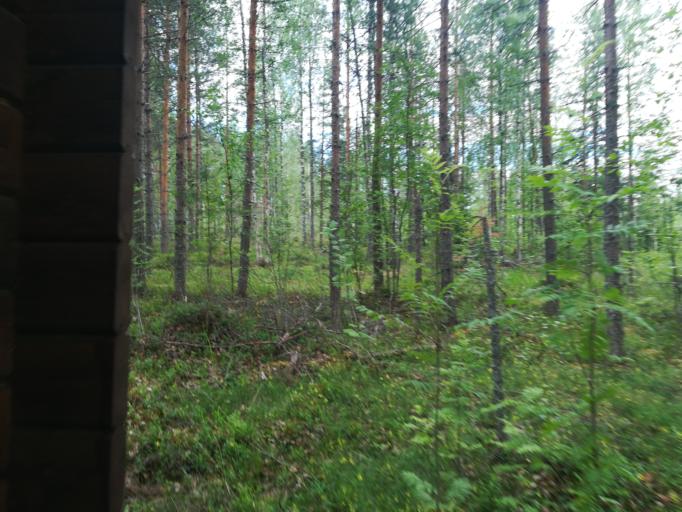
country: FI
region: South Karelia
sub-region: Lappeenranta
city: Savitaipale
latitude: 61.5027
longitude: 27.8375
